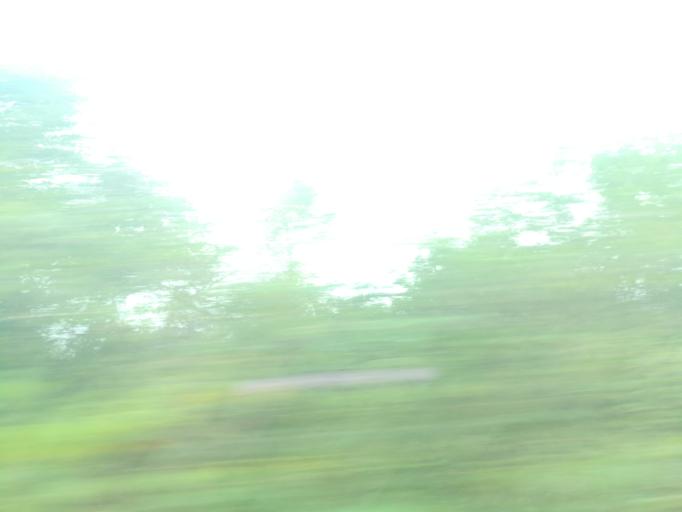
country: NG
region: Ogun
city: Ayetoro
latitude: 7.1041
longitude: 3.1461
